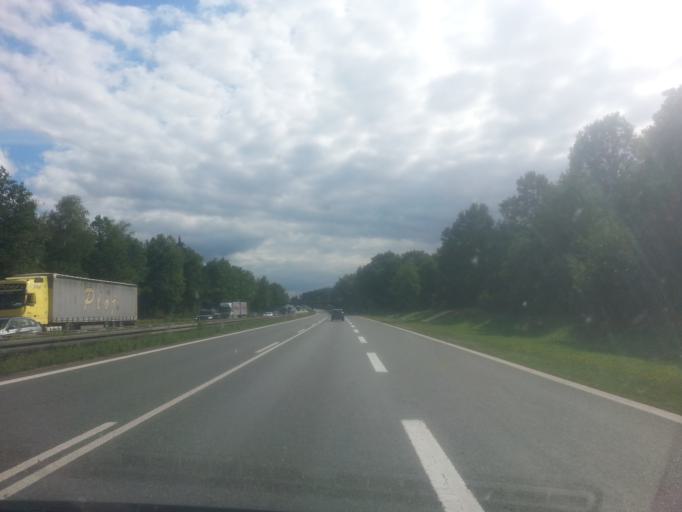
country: DE
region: Bavaria
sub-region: Upper Palatinate
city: Wackersdorf
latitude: 49.3399
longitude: 12.1499
